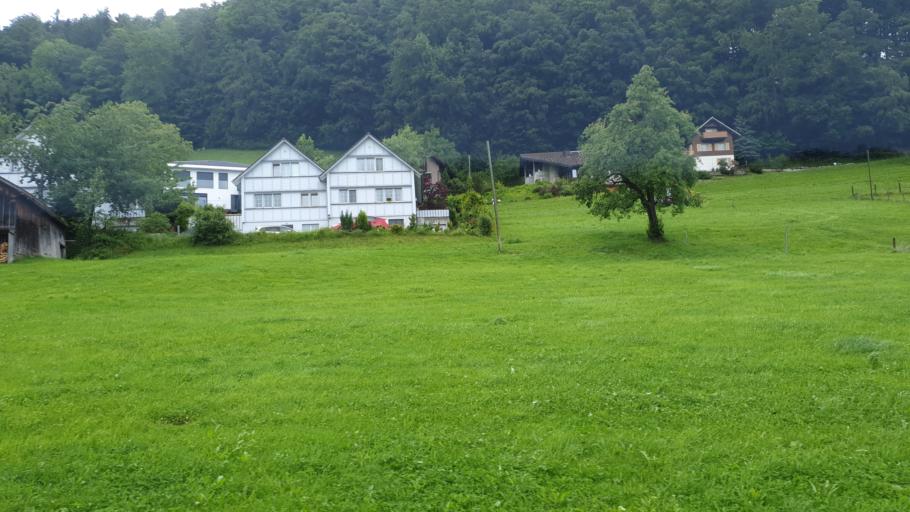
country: CH
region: Appenzell Ausserrhoden
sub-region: Bezirk Vorderland
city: Heiden
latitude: 47.4604
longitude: 9.5321
